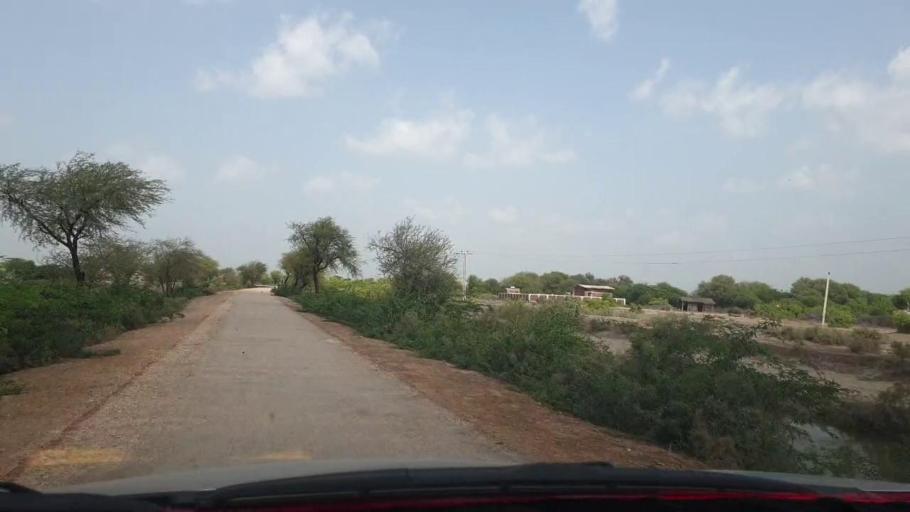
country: PK
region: Sindh
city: Rajo Khanani
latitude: 24.9186
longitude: 68.8982
